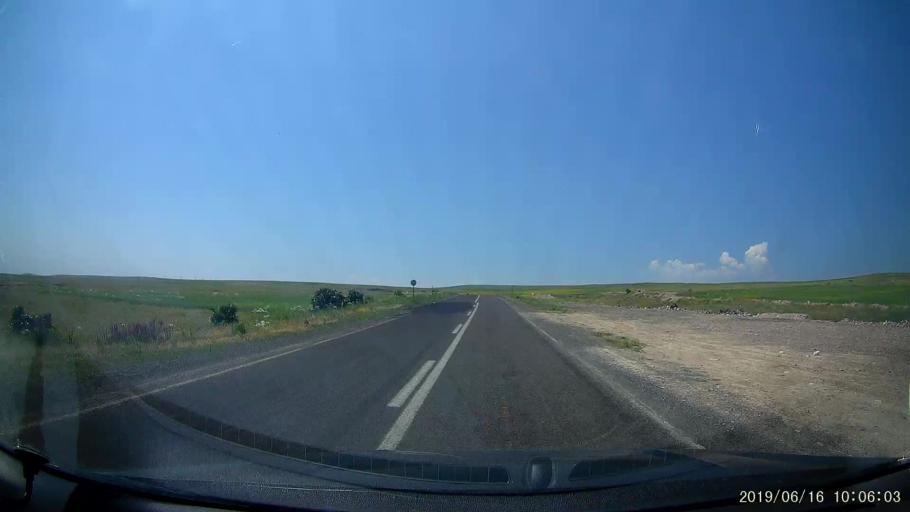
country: TR
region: Kars
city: Digor
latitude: 40.2612
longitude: 43.5408
